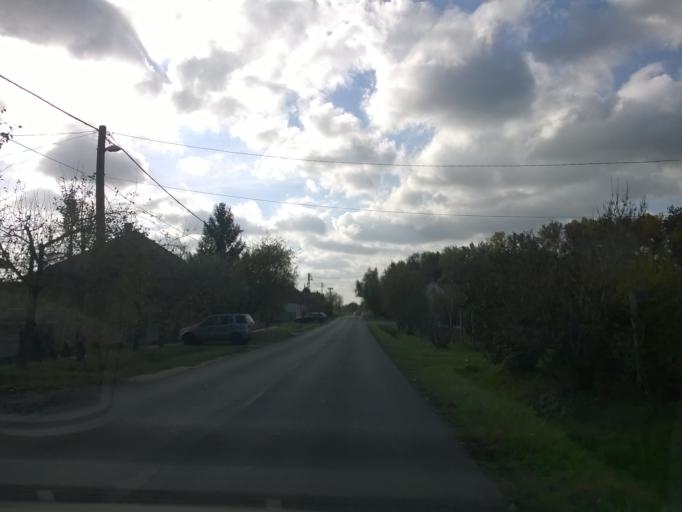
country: HU
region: Pest
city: Rackeve
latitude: 47.1254
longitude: 18.9470
